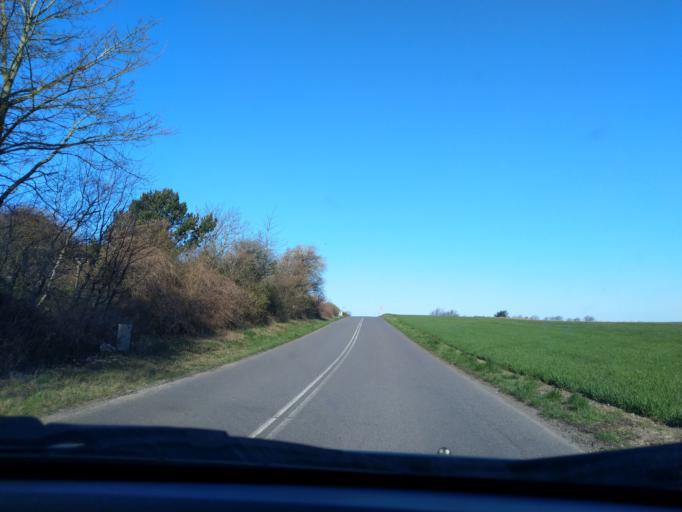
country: DK
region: Zealand
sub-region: Kalundborg Kommune
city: Kalundborg
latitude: 55.7270
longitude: 11.0000
